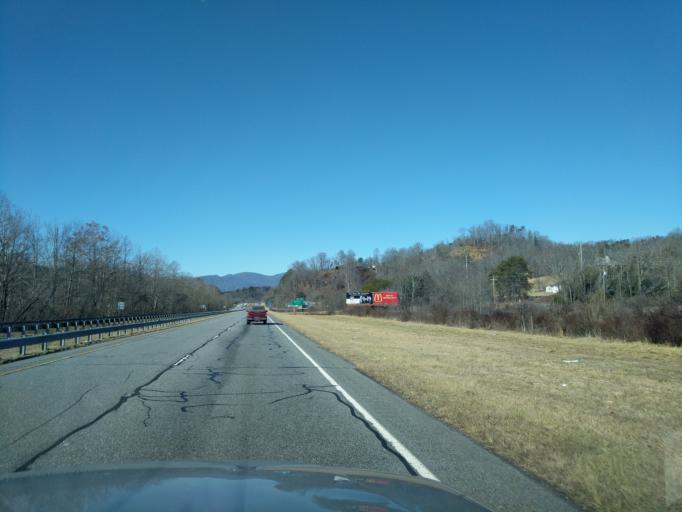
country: US
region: North Carolina
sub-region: Swain County
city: Cherokee
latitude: 35.4229
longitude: -83.3467
